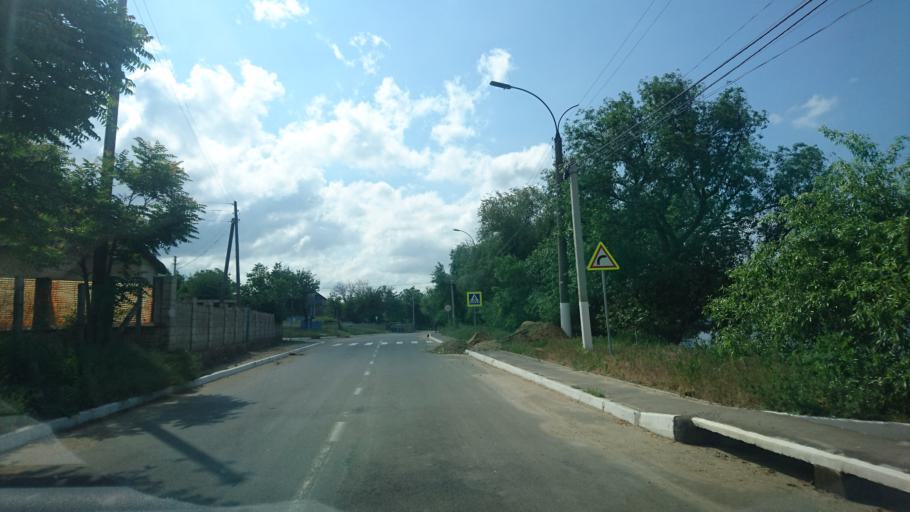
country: MD
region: Telenesti
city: Cocieri
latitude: 47.3528
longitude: 29.1070
